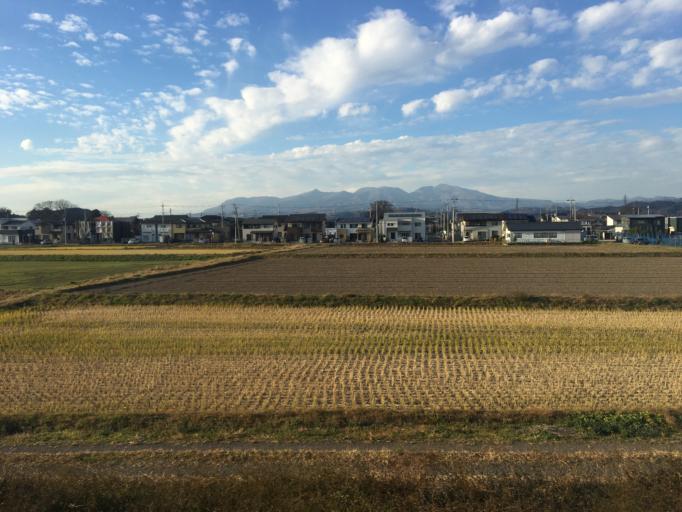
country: JP
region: Gunma
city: Kiryu
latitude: 36.3988
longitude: 139.3015
